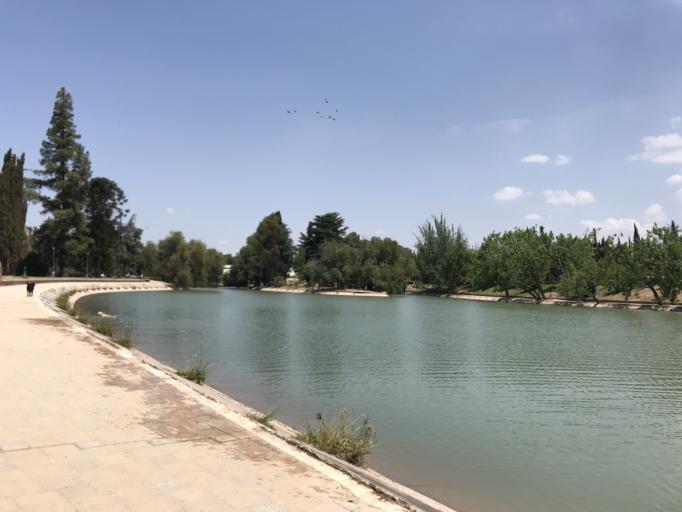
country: AR
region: Mendoza
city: Mendoza
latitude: -32.8954
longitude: -68.8645
